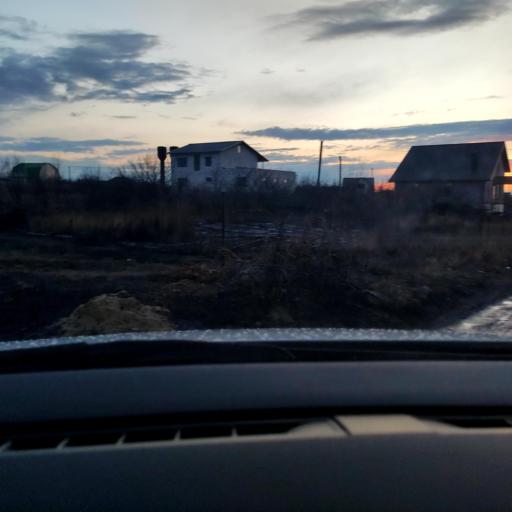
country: RU
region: Voronezj
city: Semiluki
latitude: 51.7137
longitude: 39.0175
